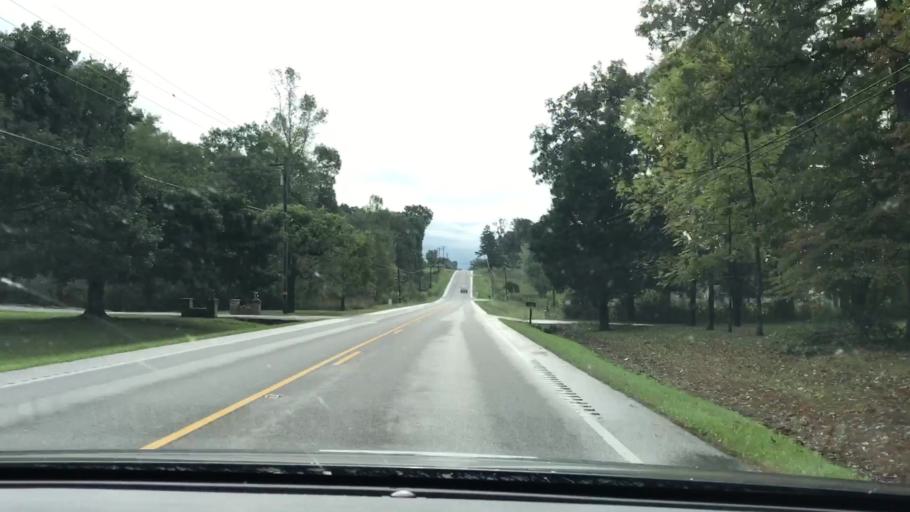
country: US
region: Tennessee
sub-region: Fentress County
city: Jamestown
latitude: 36.3708
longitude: -84.8533
